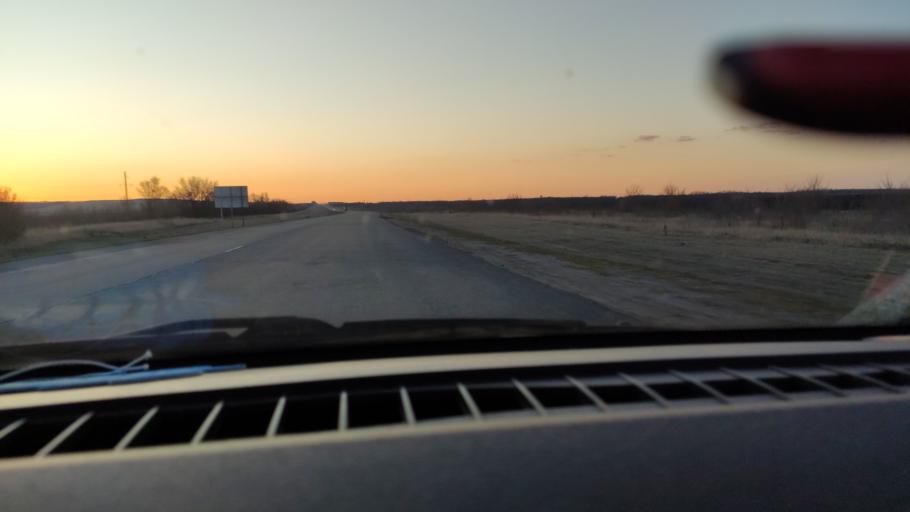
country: RU
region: Saratov
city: Yelshanka
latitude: 51.8302
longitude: 46.2414
